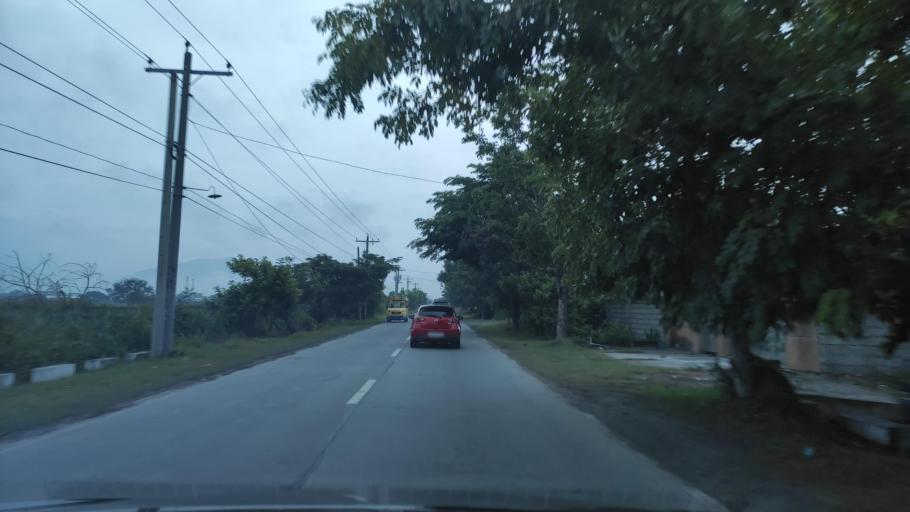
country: PH
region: Central Luzon
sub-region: Province of Pampanga
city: Santo Domingo
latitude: 15.0603
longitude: 120.7543
